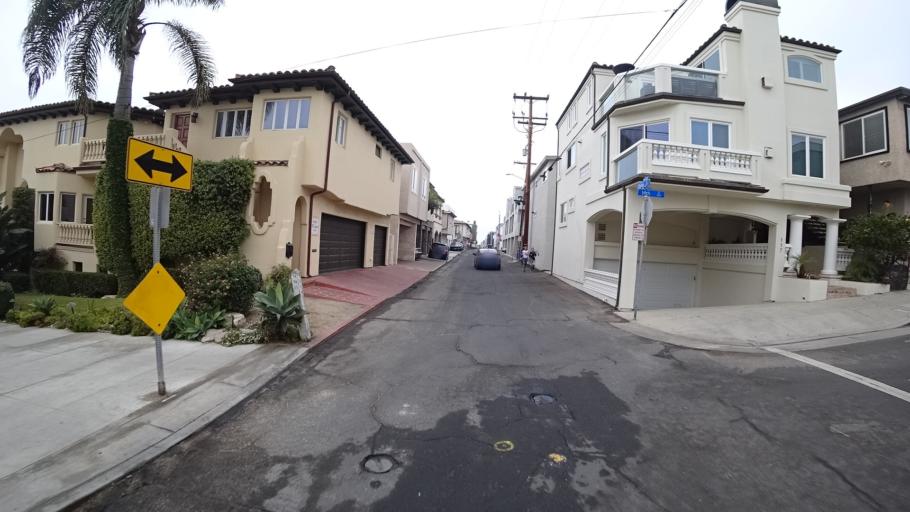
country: US
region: California
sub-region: Los Angeles County
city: Manhattan Beach
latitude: 33.8864
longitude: -118.4124
